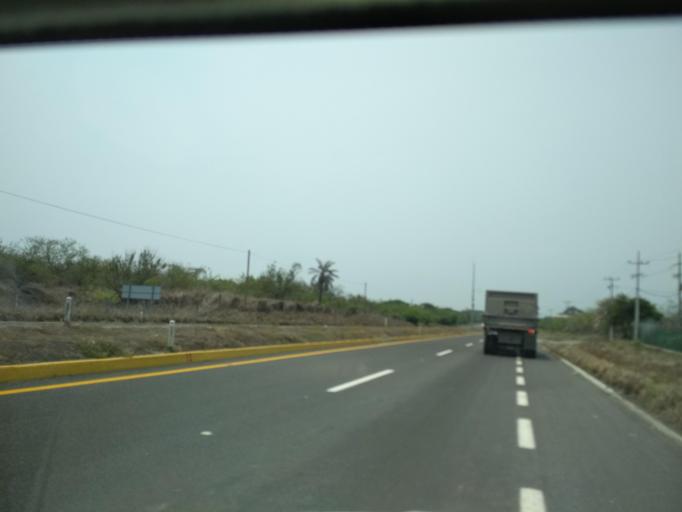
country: MX
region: Veracruz
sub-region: Veracruz
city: Delfino Victoria (Santa Fe)
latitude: 19.2264
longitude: -96.2582
